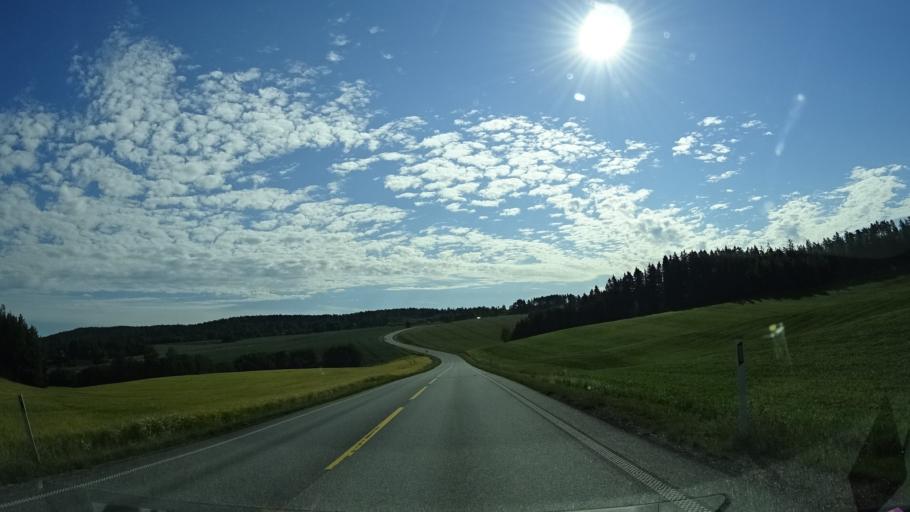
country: NO
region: Ostfold
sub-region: Eidsberg
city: Mysen
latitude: 59.5540
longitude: 11.3878
